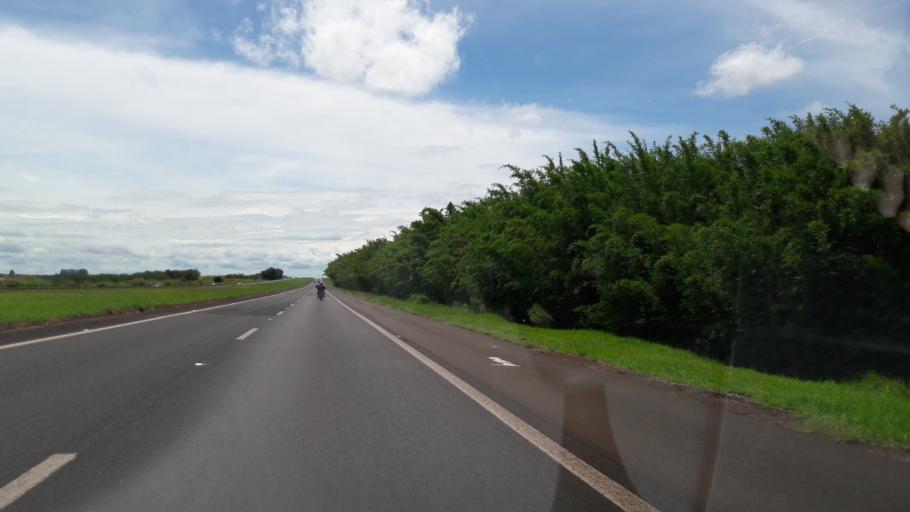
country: BR
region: Sao Paulo
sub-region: Avare
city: Avare
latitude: -22.9504
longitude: -48.8803
